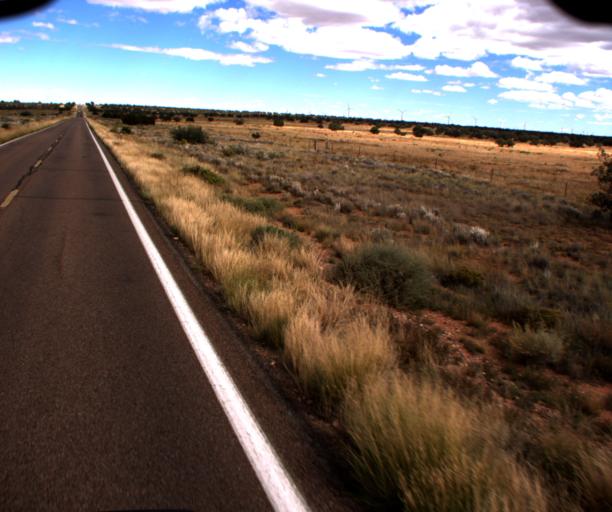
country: US
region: Arizona
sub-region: Navajo County
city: Snowflake
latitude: 34.6515
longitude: -110.3418
